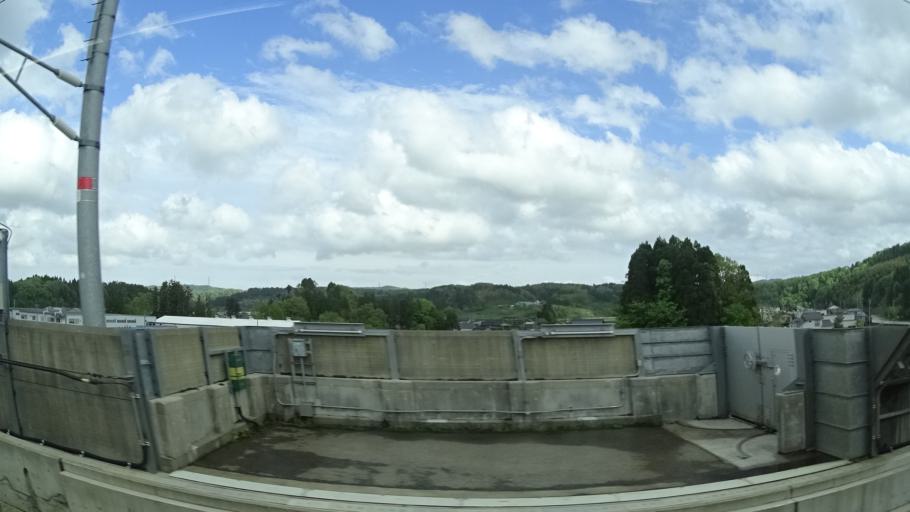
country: JP
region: Ishikawa
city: Tsubata
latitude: 36.6617
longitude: 136.7517
